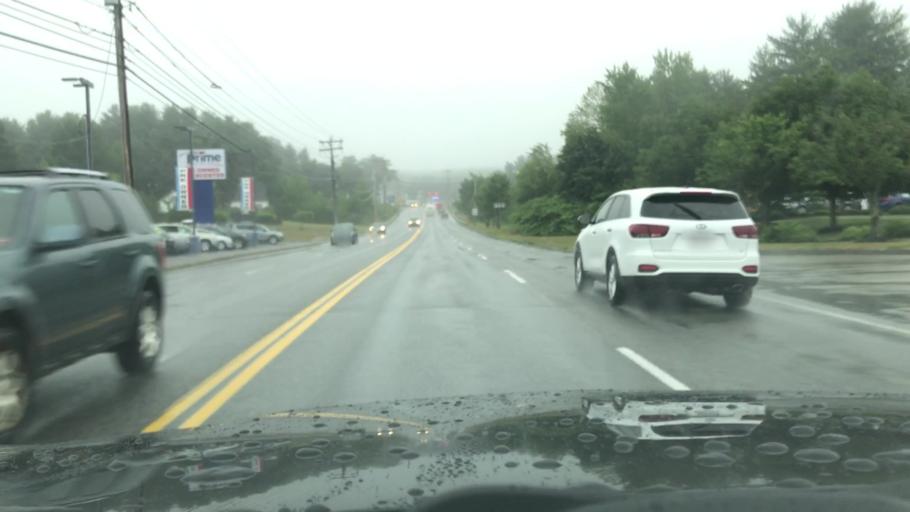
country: US
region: Maine
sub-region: York County
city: Saco
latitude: 43.5299
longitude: -70.4261
